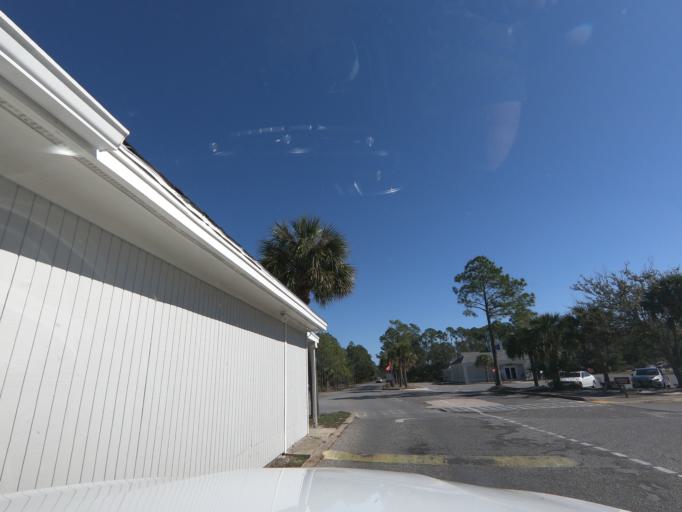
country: US
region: Florida
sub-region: Bay County
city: Lower Grand Lagoon
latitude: 30.1352
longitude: -85.7423
